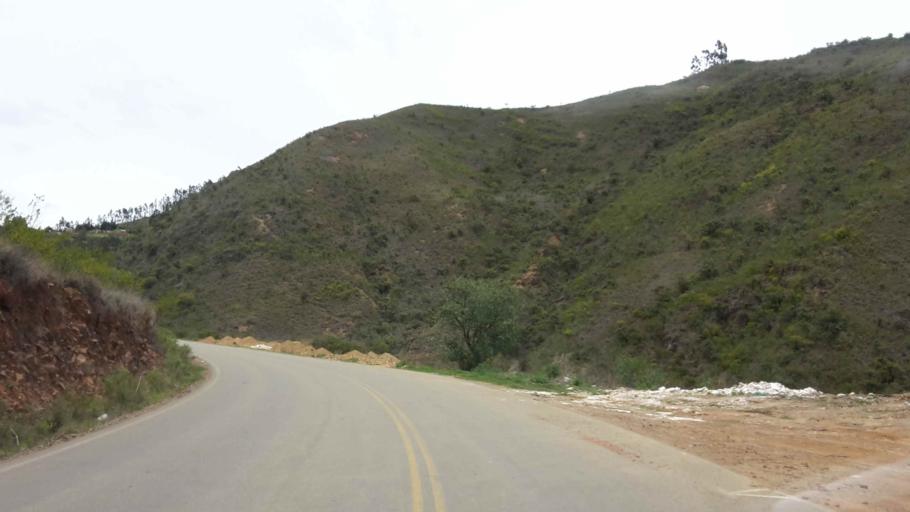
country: BO
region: Cochabamba
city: Totora
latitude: -17.7256
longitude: -65.1919
